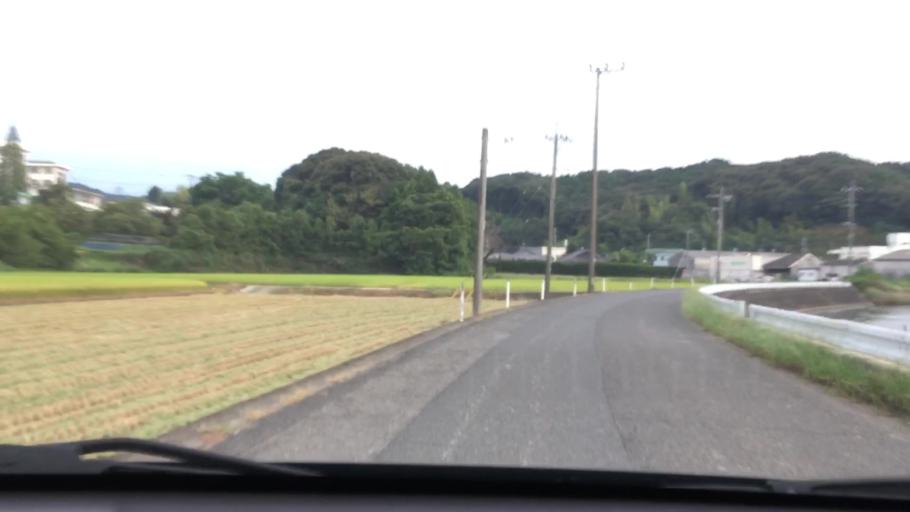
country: JP
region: Nagasaki
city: Togitsu
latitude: 32.9901
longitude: 129.7733
